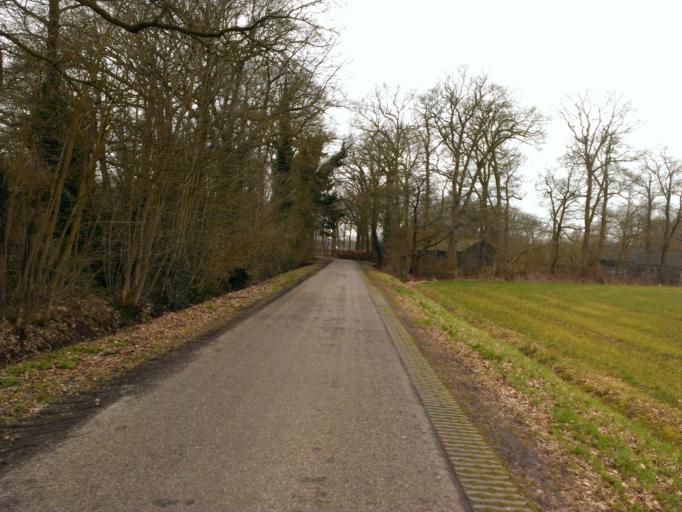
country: NL
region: Drenthe
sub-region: Gemeente Hoogeveen
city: Hoogeveen
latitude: 52.7625
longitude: 6.4586
